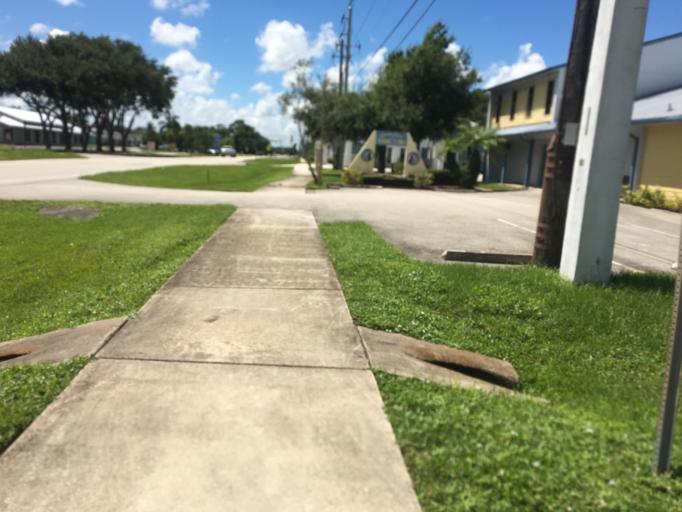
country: US
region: Florida
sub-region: Martin County
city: Palm City
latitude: 27.1675
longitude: -80.2695
